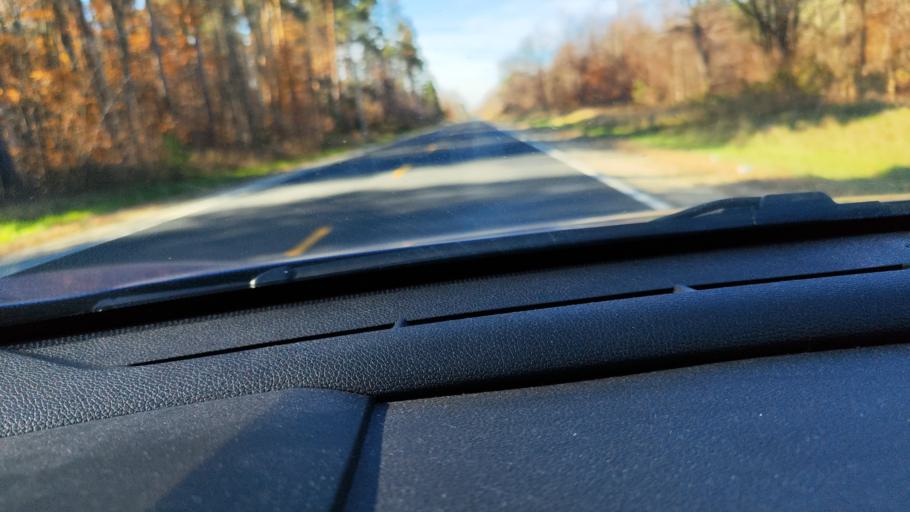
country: CA
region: Ontario
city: Angus
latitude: 44.3546
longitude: -79.9890
